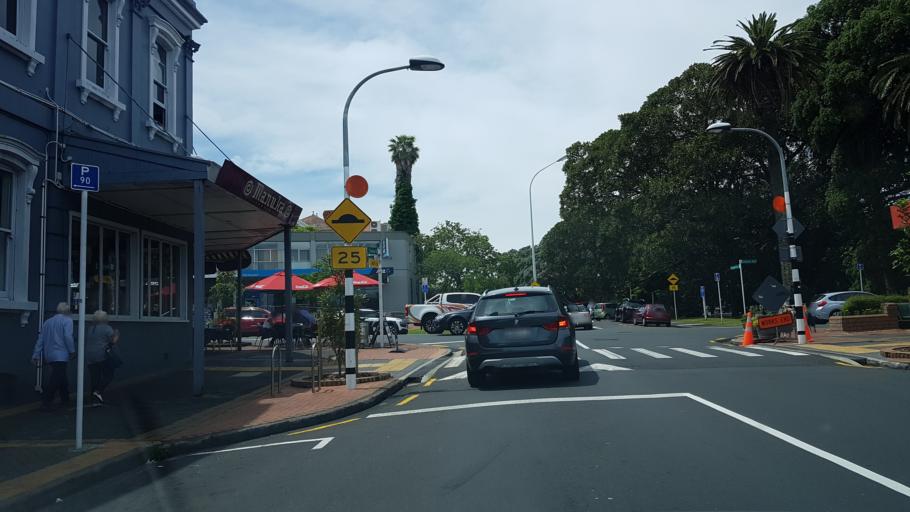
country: NZ
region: Auckland
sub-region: Auckland
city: Auckland
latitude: -36.8306
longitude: 174.7971
